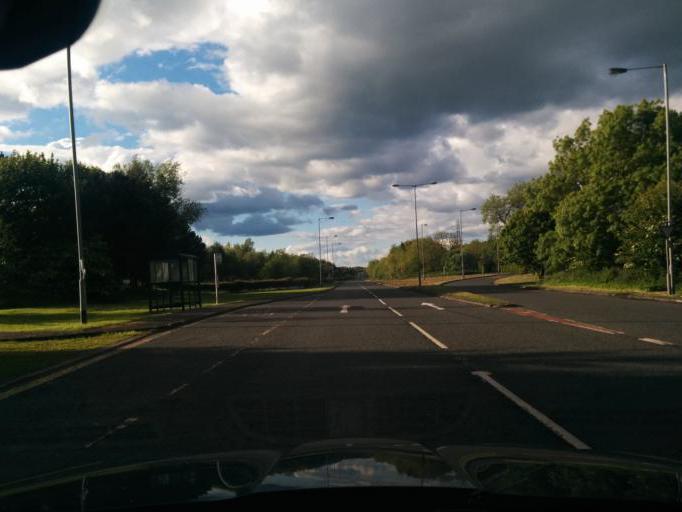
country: GB
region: England
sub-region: Northumberland
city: Cramlington
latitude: 55.0997
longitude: -1.6181
